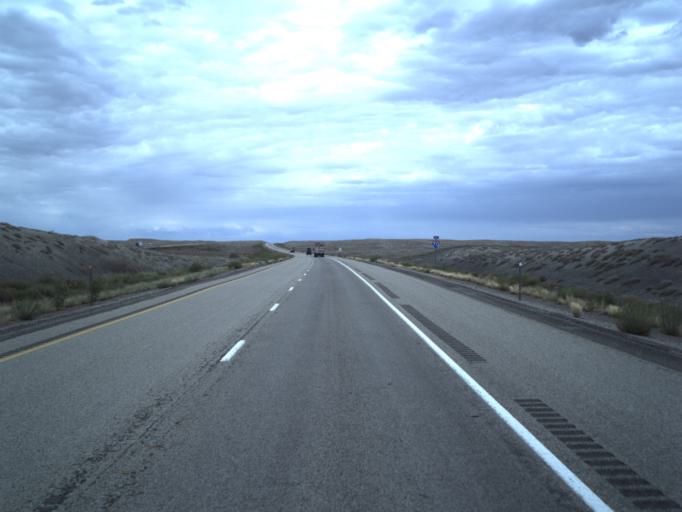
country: US
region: Utah
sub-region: Grand County
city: Moab
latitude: 38.9805
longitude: -109.3443
